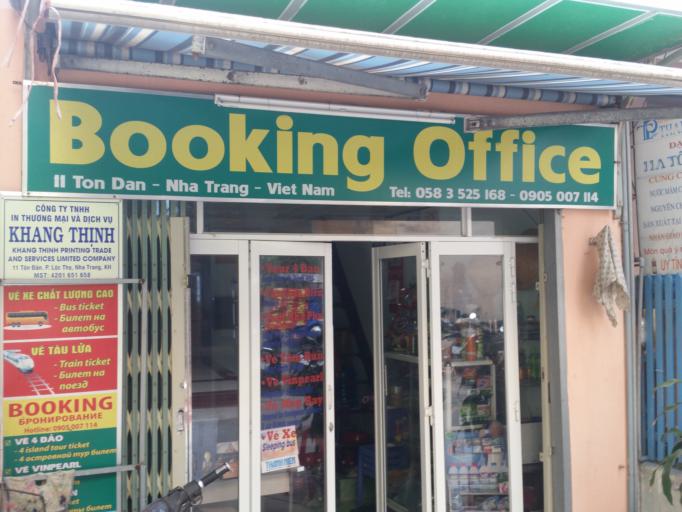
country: VN
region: Khanh Hoa
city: Nha Trang
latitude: 12.2380
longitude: 109.1963
